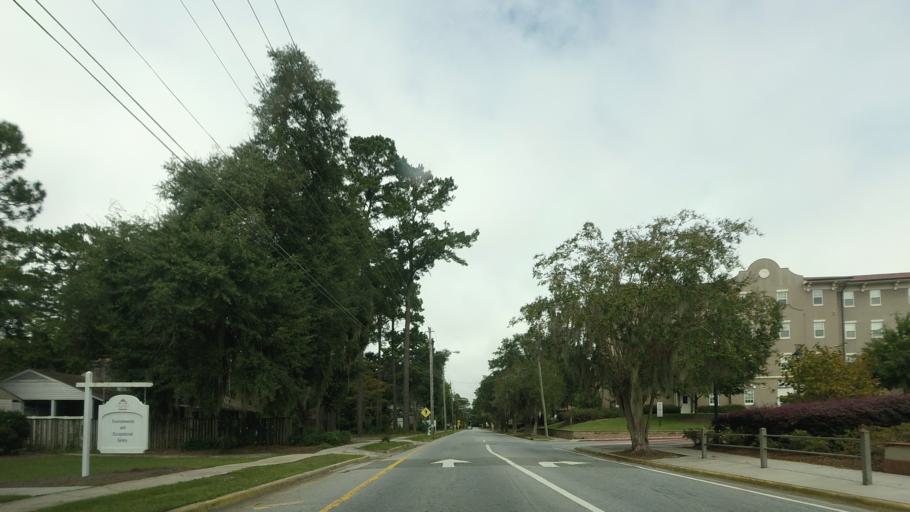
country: US
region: Georgia
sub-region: Lowndes County
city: Valdosta
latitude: 30.8474
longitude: -83.2909
